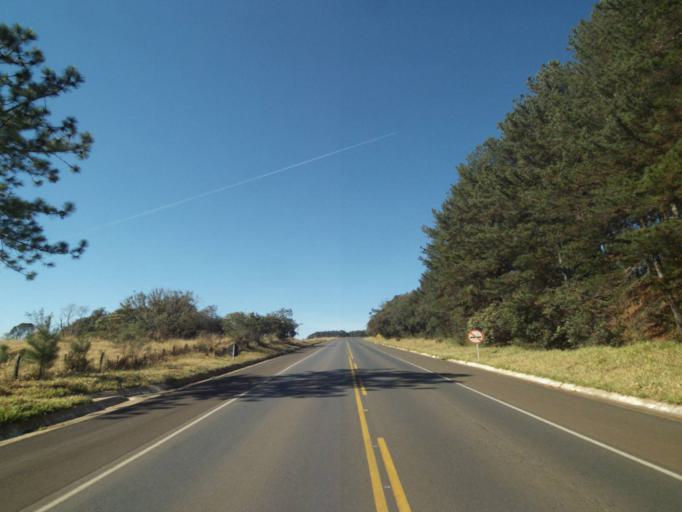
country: BR
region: Parana
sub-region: Tibagi
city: Tibagi
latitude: -24.4840
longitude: -50.4406
